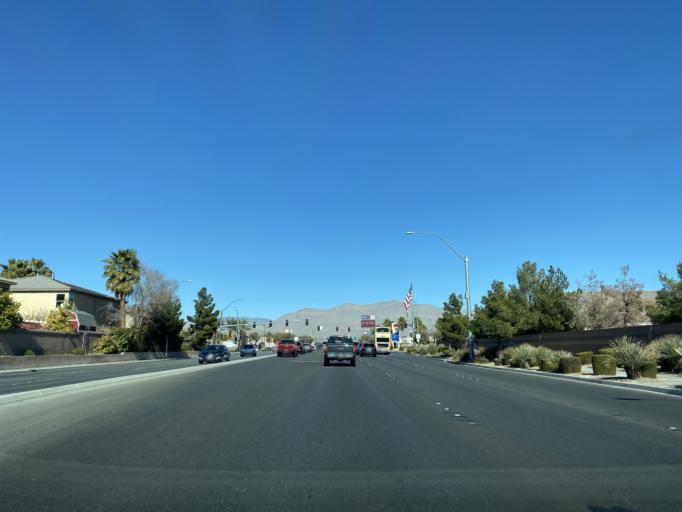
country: US
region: Nevada
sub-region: Clark County
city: North Las Vegas
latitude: 36.2678
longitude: -115.2068
